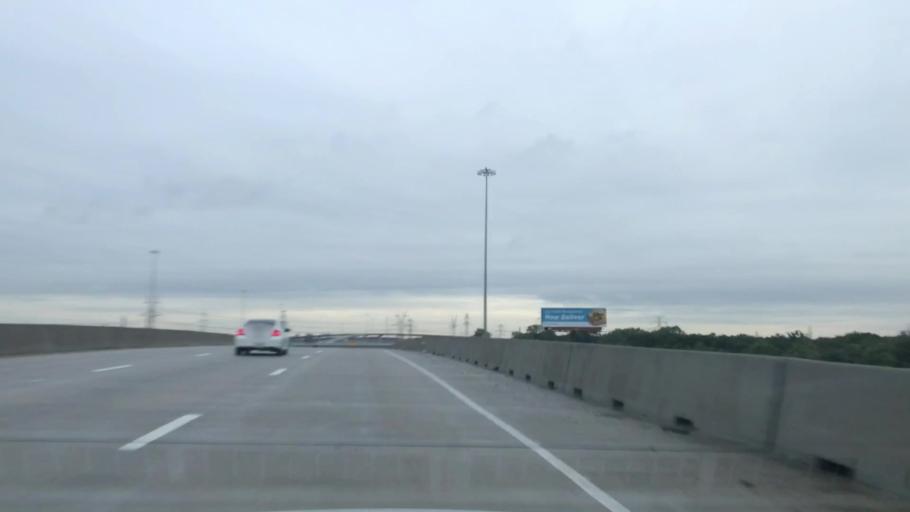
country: US
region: Texas
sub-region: Dallas County
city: Carrollton
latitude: 32.9930
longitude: -96.9478
